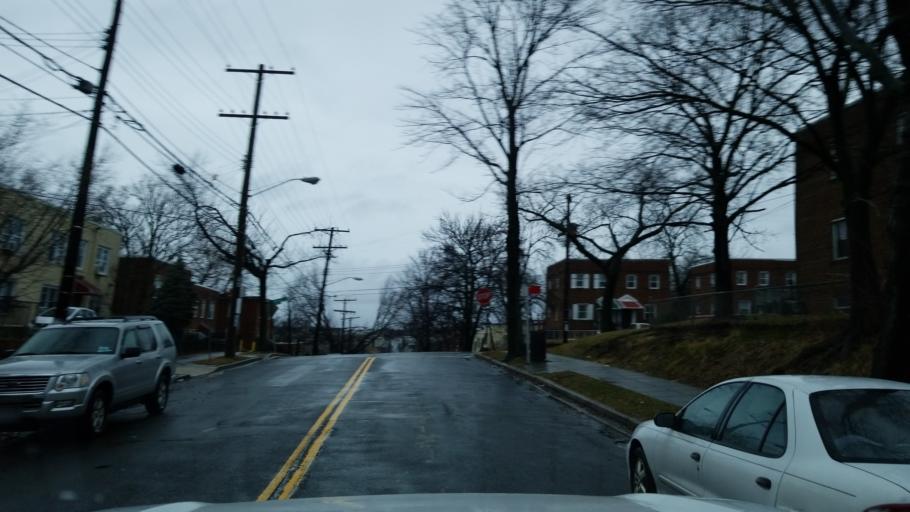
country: US
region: Maryland
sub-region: Prince George's County
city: Glassmanor
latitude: 38.8297
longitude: -77.0006
